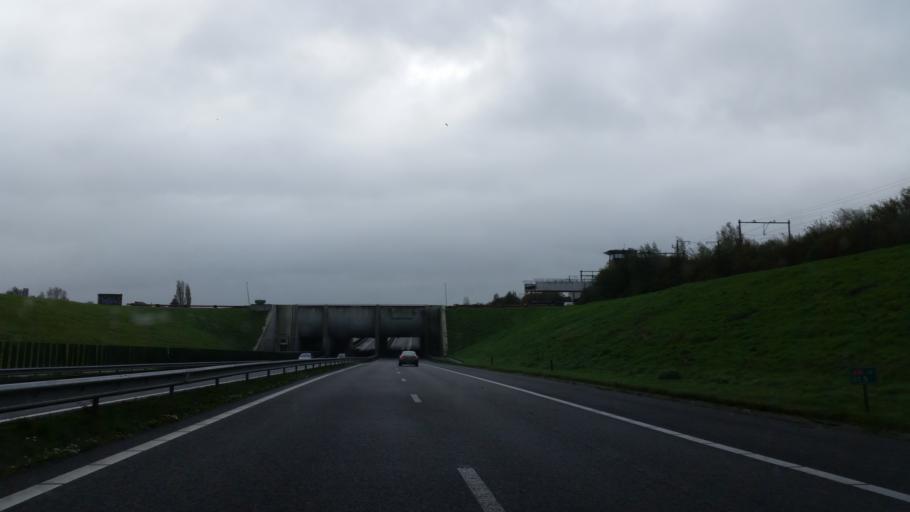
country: NL
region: Friesland
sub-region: Gemeente Boarnsterhim
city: Grou
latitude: 53.0811
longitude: 5.8279
